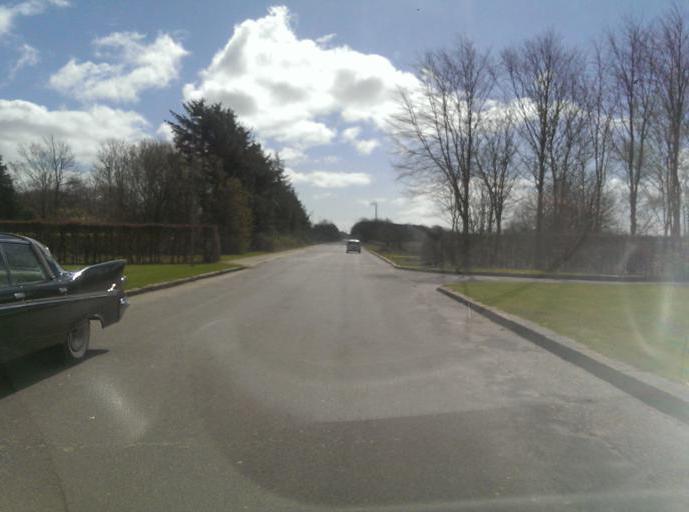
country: DK
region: South Denmark
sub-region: Esbjerg Kommune
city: Esbjerg
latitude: 55.4899
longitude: 8.4170
